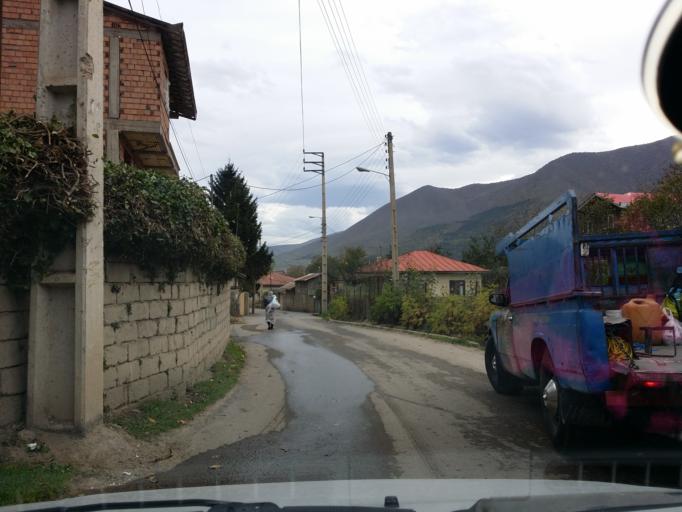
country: IR
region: Mazandaran
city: `Abbasabad
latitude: 36.5041
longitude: 51.1479
